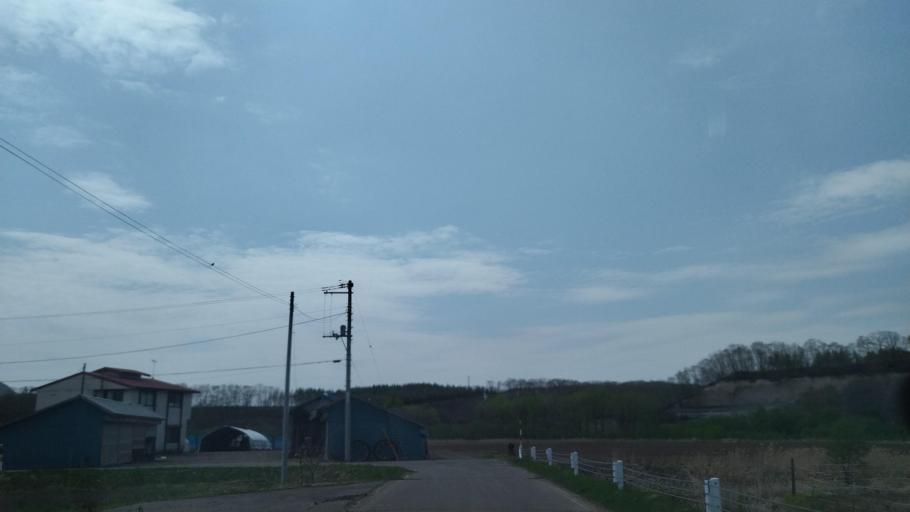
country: JP
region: Hokkaido
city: Otofuke
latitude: 43.3163
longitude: 143.5735
